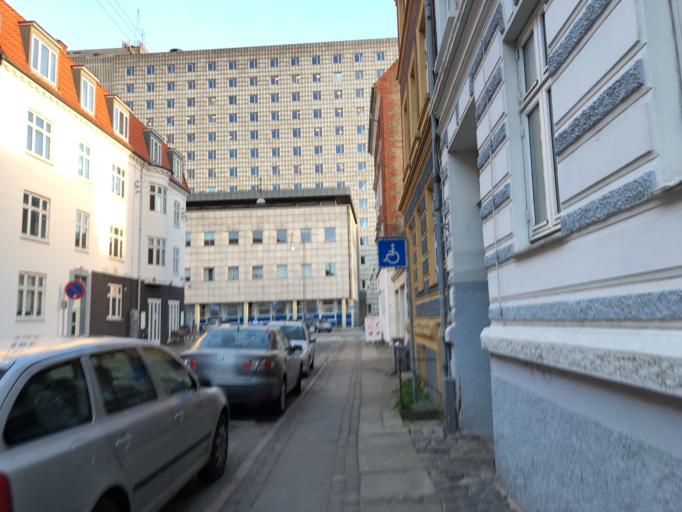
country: DK
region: North Denmark
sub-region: Alborg Kommune
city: Aalborg
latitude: 57.0500
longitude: 9.9121
